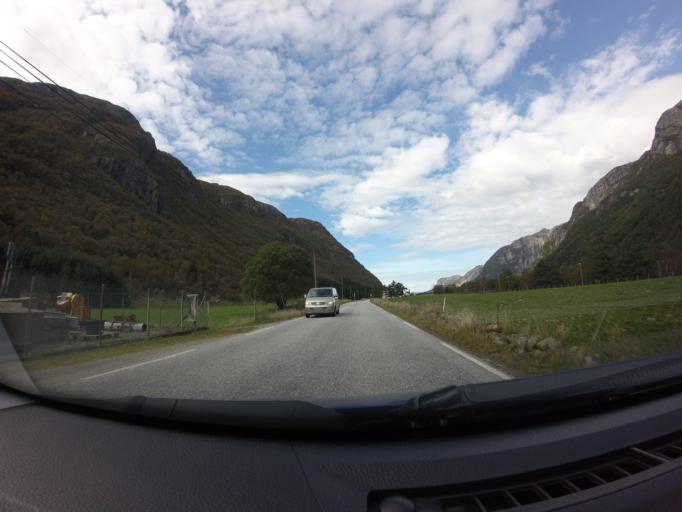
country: NO
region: Rogaland
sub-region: Forsand
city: Forsand
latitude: 58.8220
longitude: 6.1996
